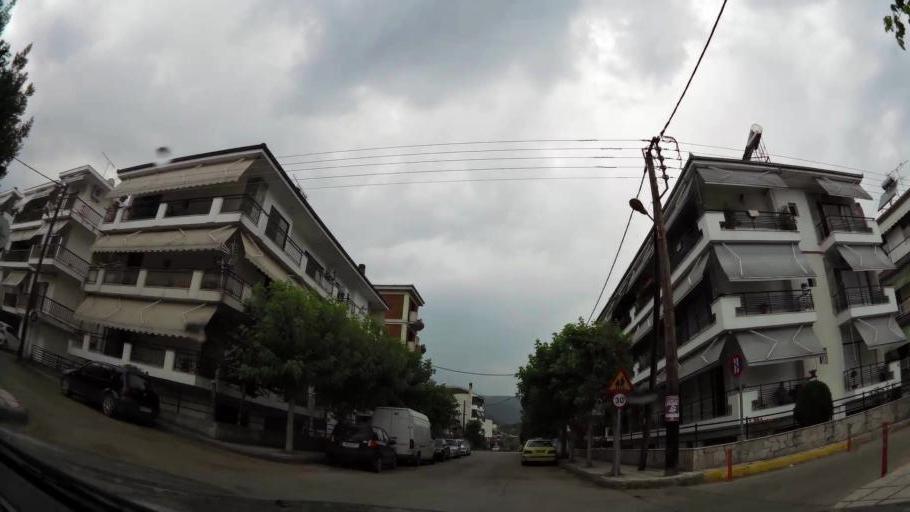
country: GR
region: Central Macedonia
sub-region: Nomos Imathias
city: Veroia
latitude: 40.5285
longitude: 22.1974
